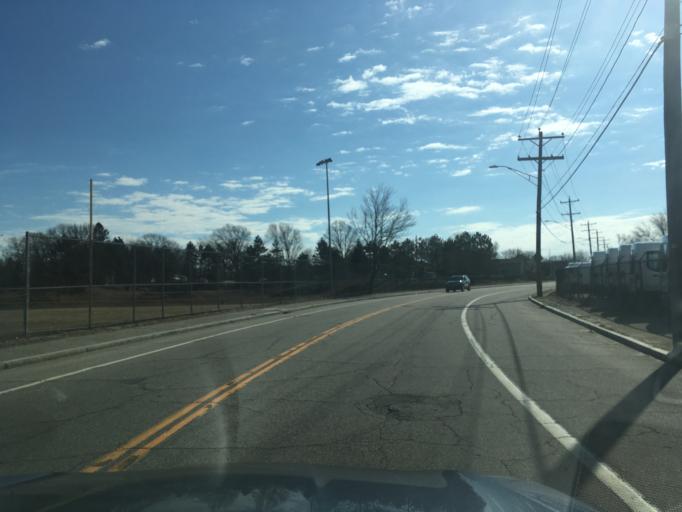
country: US
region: Rhode Island
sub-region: Providence County
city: Cranston
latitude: 41.7933
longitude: -71.4377
